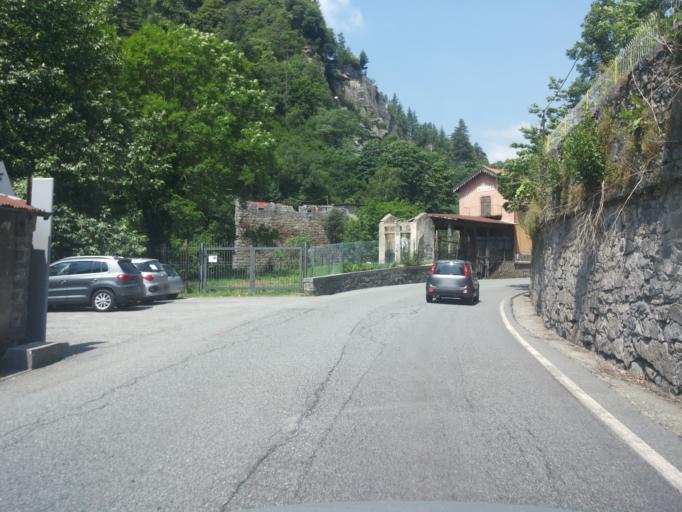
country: IT
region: Piedmont
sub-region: Provincia di Biella
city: San Paolo Cervo
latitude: 45.6480
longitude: 8.0164
